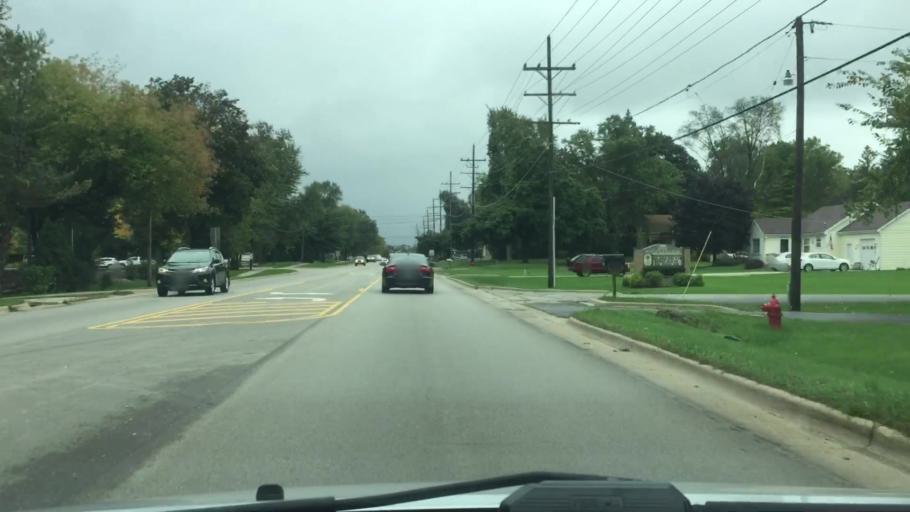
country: US
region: Illinois
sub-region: McHenry County
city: McHenry
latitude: 42.3352
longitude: -88.2746
